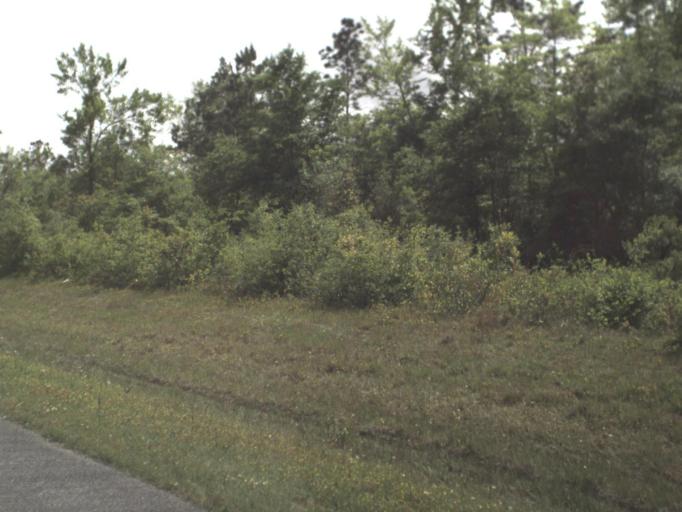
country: US
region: Florida
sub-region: Santa Rosa County
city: Wallace
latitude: 30.8266
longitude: -87.1374
